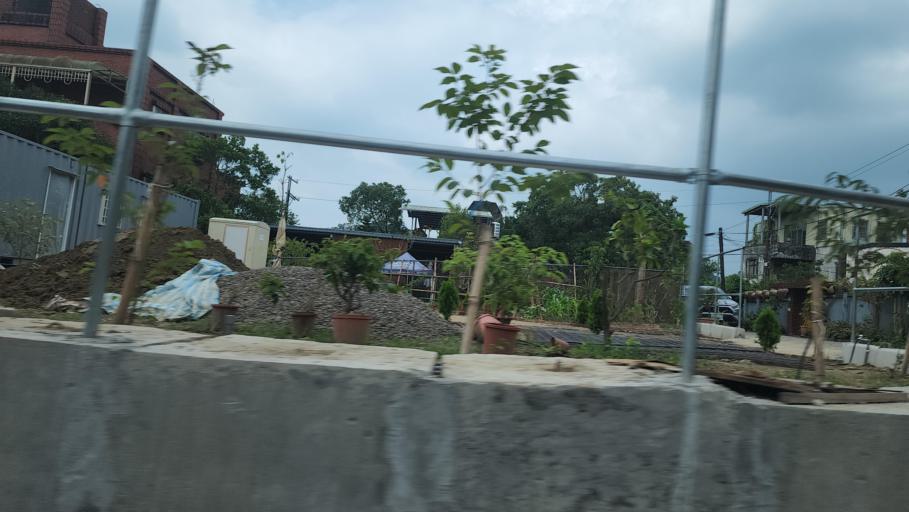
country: TW
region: Taiwan
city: Daxi
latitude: 24.9078
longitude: 121.3909
